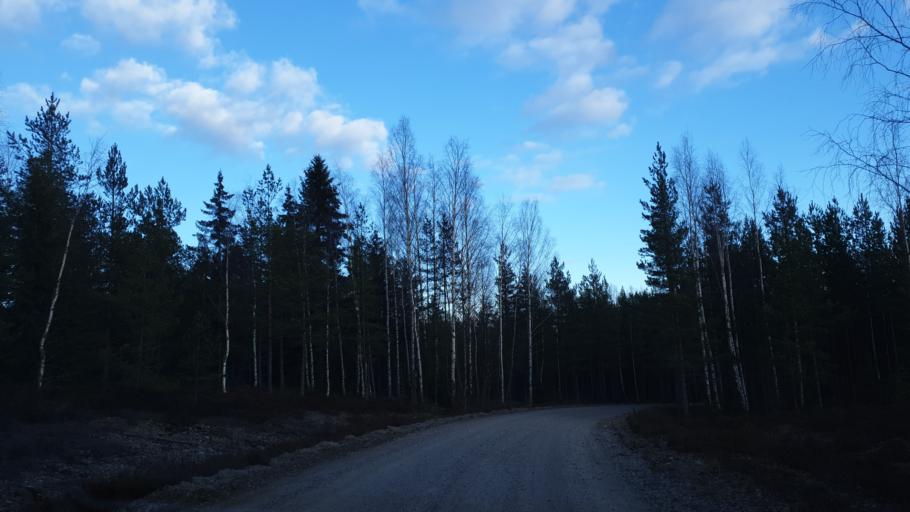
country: SE
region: OErebro
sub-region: Orebro Kommun
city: Garphyttan
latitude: 59.3618
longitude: 14.9775
